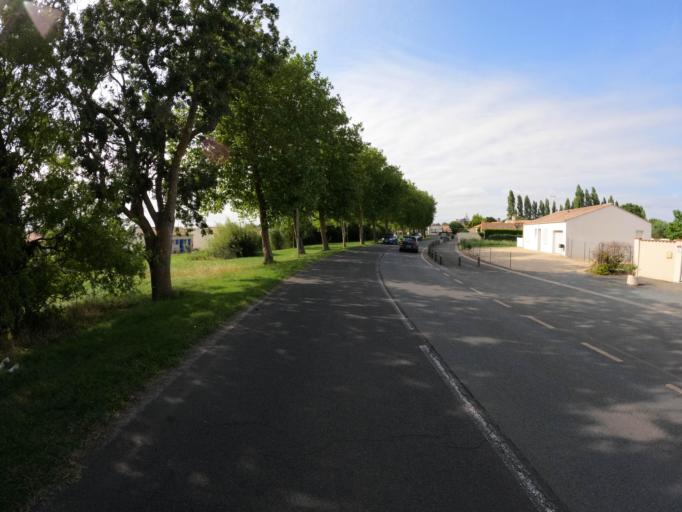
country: FR
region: Pays de la Loire
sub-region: Departement de la Vendee
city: Triaize
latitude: 46.3603
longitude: -1.2417
